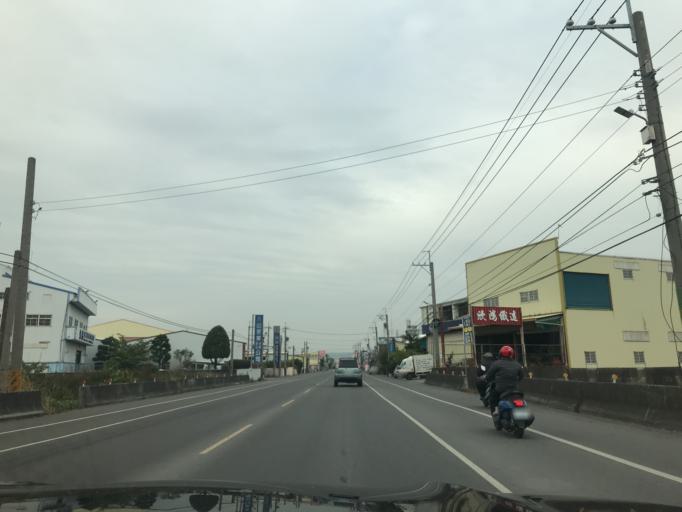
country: TW
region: Taiwan
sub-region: Nantou
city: Nantou
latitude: 23.9099
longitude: 120.5831
